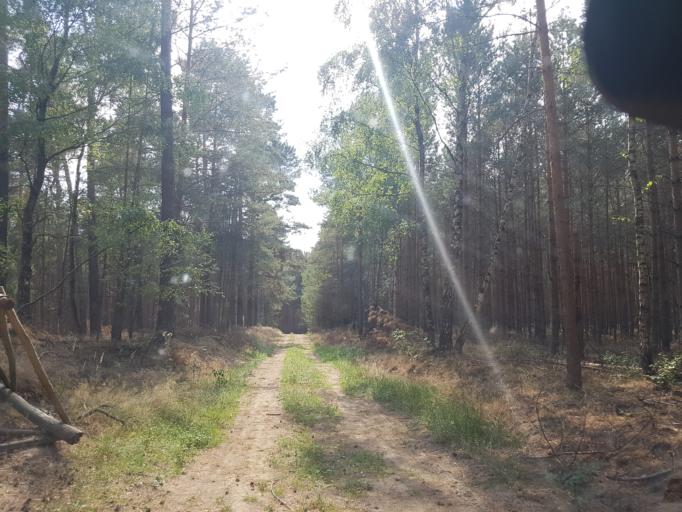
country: DE
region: Brandenburg
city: Treuenbrietzen
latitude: 52.0263
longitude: 12.8827
